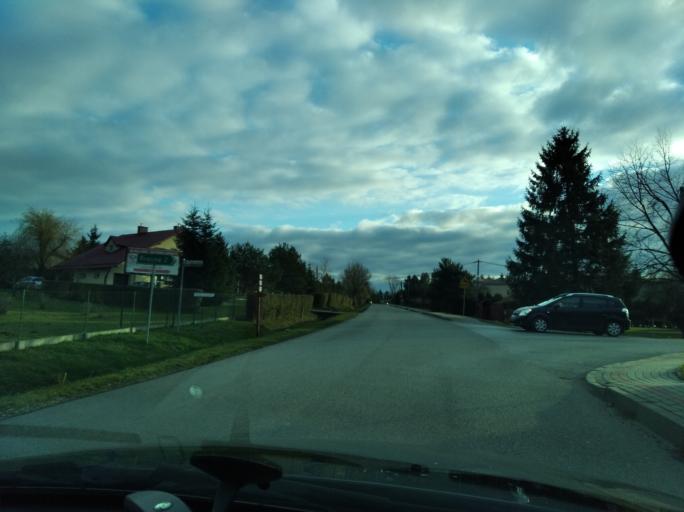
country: PL
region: Subcarpathian Voivodeship
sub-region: Powiat rzeszowski
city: Krasne
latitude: 50.0613
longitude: 22.1186
